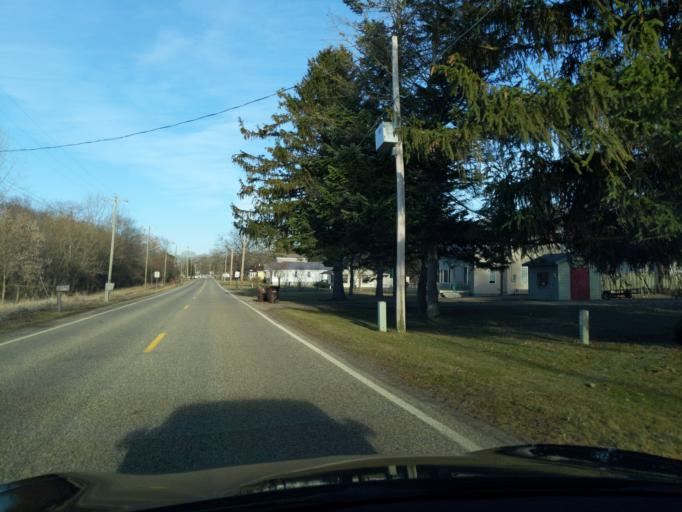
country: US
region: Michigan
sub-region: Ionia County
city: Ionia
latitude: 42.9661
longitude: -85.0788
